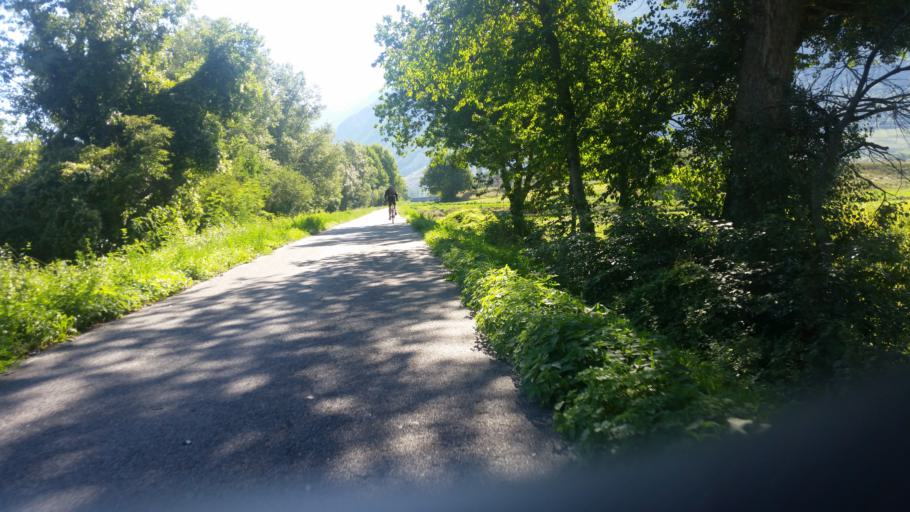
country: CH
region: Valais
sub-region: Sion District
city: Saint-Leonard
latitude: 46.2441
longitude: 7.4011
